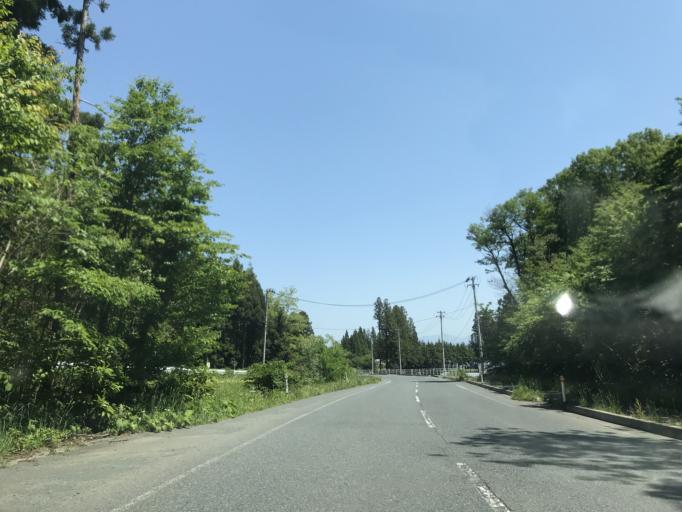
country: JP
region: Iwate
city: Kitakami
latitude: 39.2174
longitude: 141.0645
